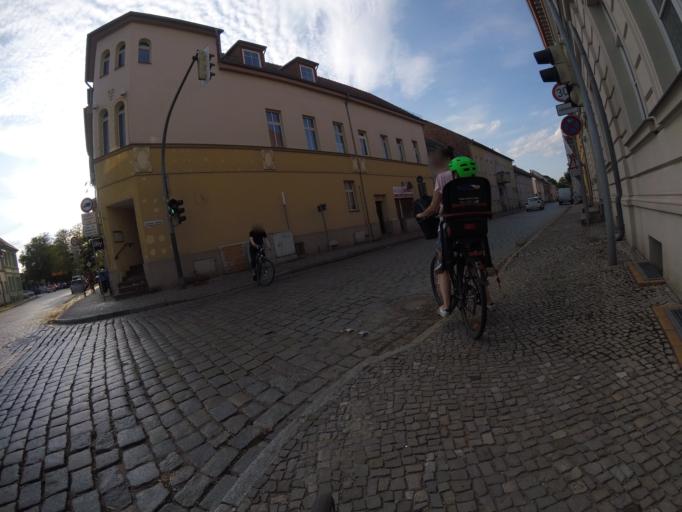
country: DE
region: Brandenburg
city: Altlandsberg
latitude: 52.5649
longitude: 13.7280
